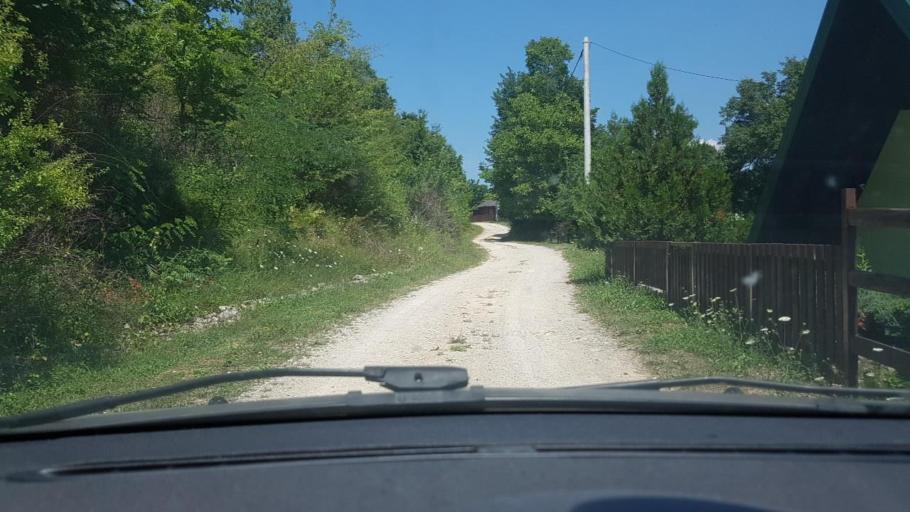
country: BA
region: Federation of Bosnia and Herzegovina
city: Orasac
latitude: 44.5653
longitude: 16.0801
